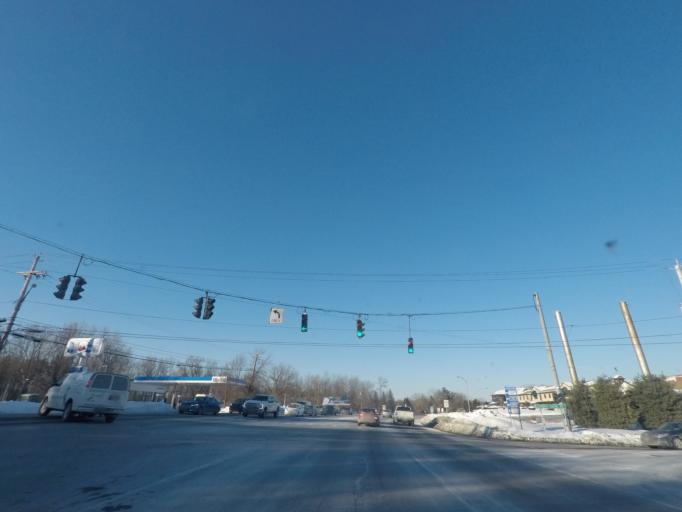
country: US
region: New York
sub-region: Saratoga County
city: Saratoga Springs
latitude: 43.0263
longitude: -73.7924
